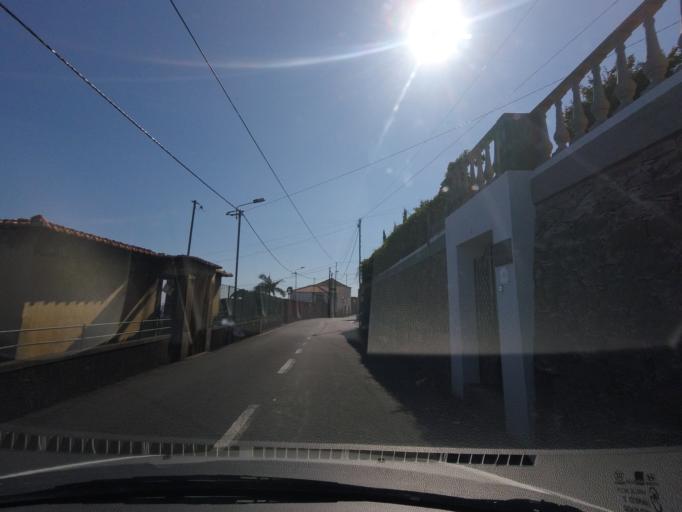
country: PT
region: Madeira
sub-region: Funchal
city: Nossa Senhora do Monte
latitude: 32.6642
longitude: -16.9043
